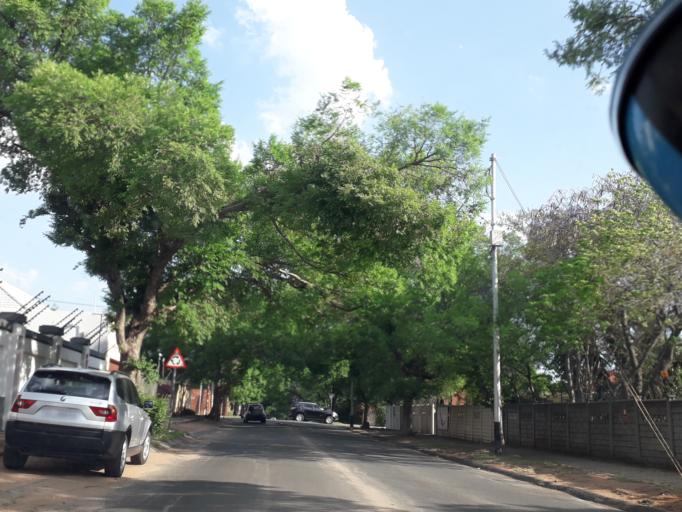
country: ZA
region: Gauteng
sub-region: City of Johannesburg Metropolitan Municipality
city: Johannesburg
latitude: -26.1415
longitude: 28.0798
